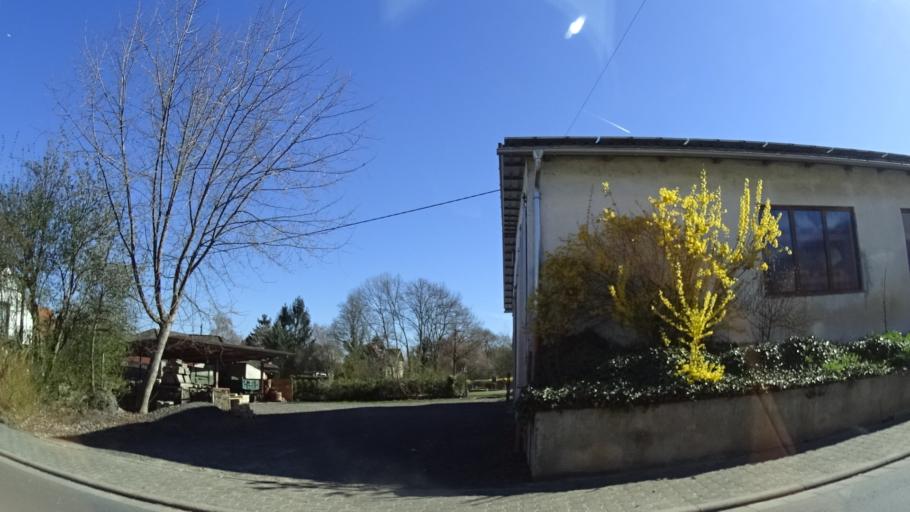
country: DE
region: Rheinland-Pfalz
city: Friesenheim
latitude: 49.8366
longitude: 8.2573
